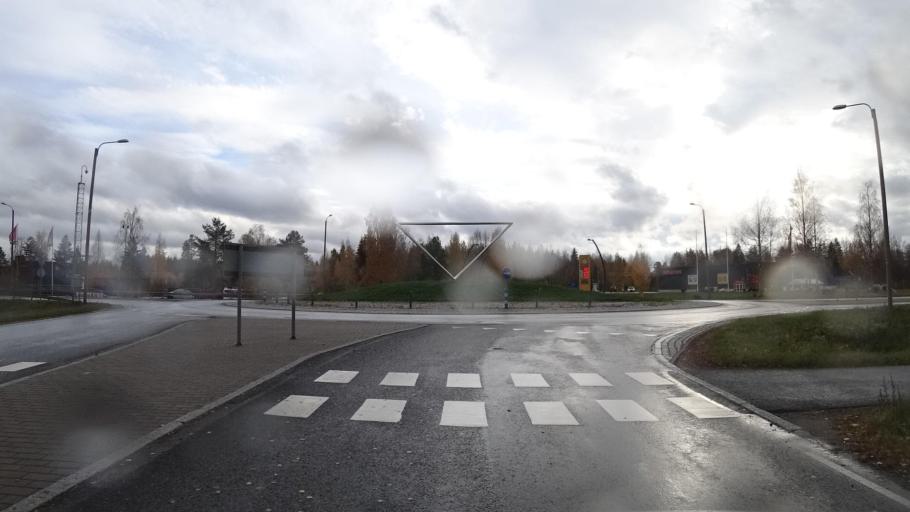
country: FI
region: Southern Savonia
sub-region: Mikkeli
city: Kangasniemi
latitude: 62.0035
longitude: 26.6573
